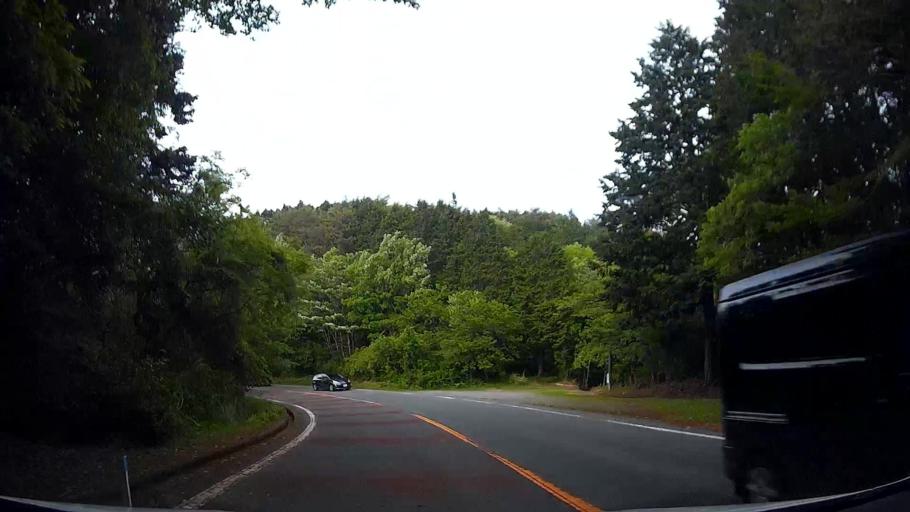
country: JP
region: Shizuoka
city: Ito
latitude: 35.0113
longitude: 139.0461
